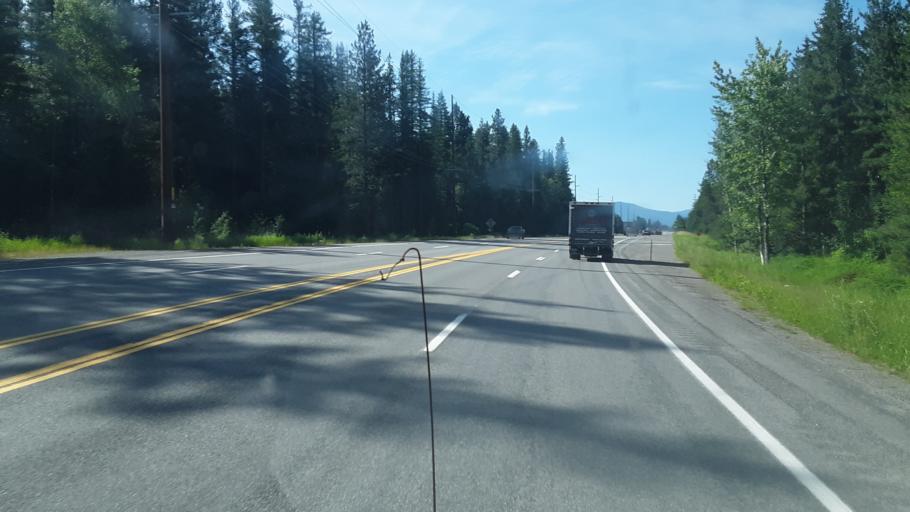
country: US
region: Idaho
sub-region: Bonner County
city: Ponderay
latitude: 48.3265
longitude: -116.5465
